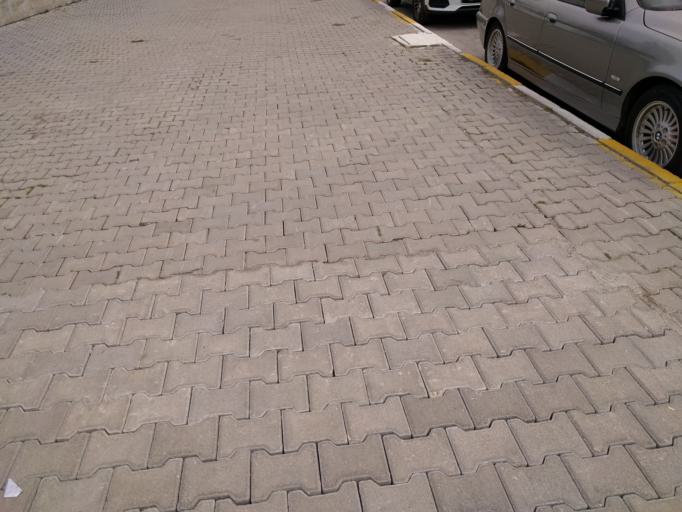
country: TR
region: Antalya
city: Antalya
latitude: 36.8609
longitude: 30.6363
